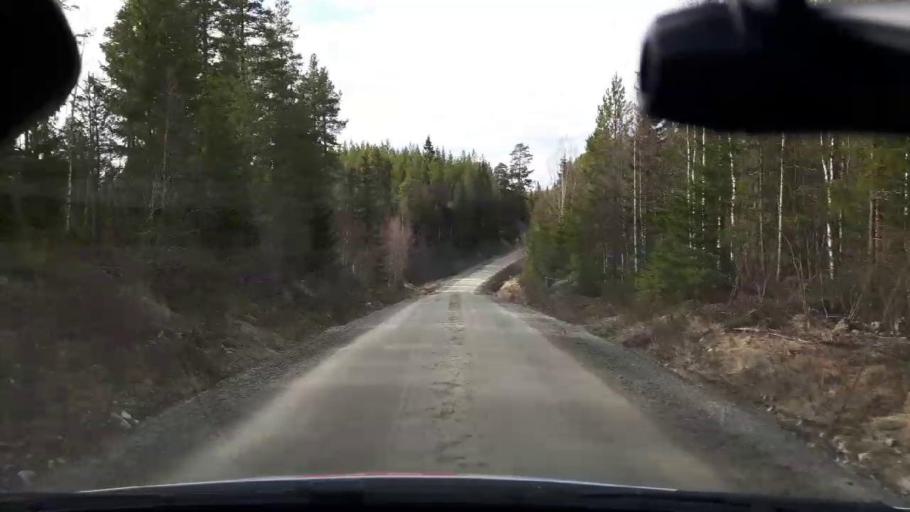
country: SE
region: Jaemtland
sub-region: Bergs Kommun
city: Hoverberg
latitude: 62.8920
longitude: 14.6559
